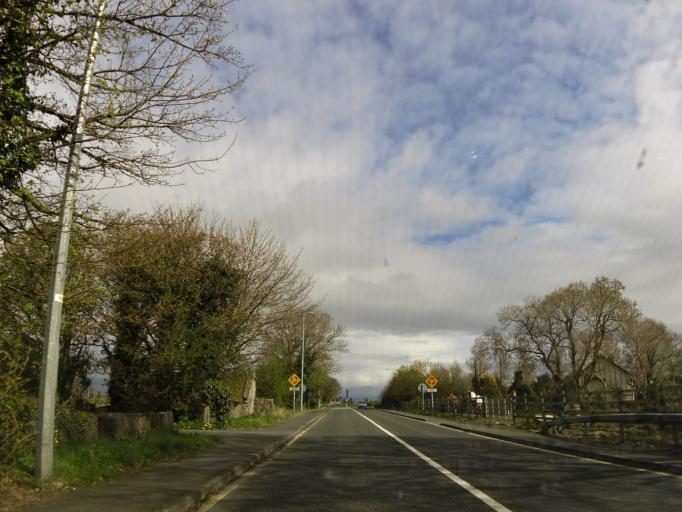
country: IE
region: Connaught
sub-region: Sligo
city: Tobercurry
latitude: 53.9538
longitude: -8.7932
